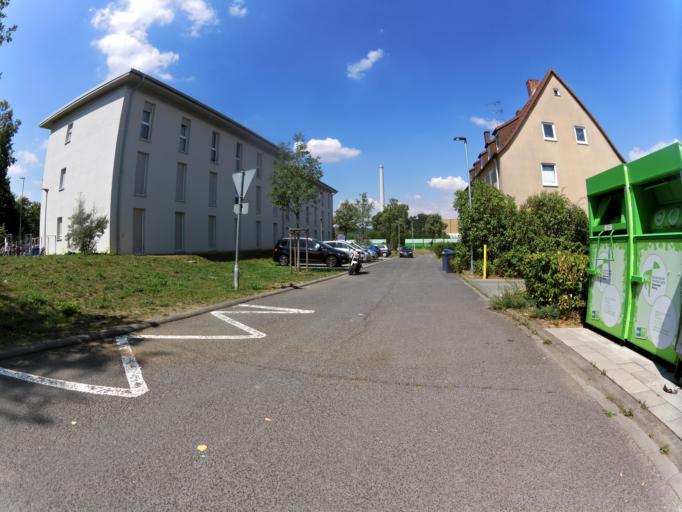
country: DE
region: Bavaria
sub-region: Regierungsbezirk Unterfranken
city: Frickenhausen
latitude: 49.6628
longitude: 10.0815
